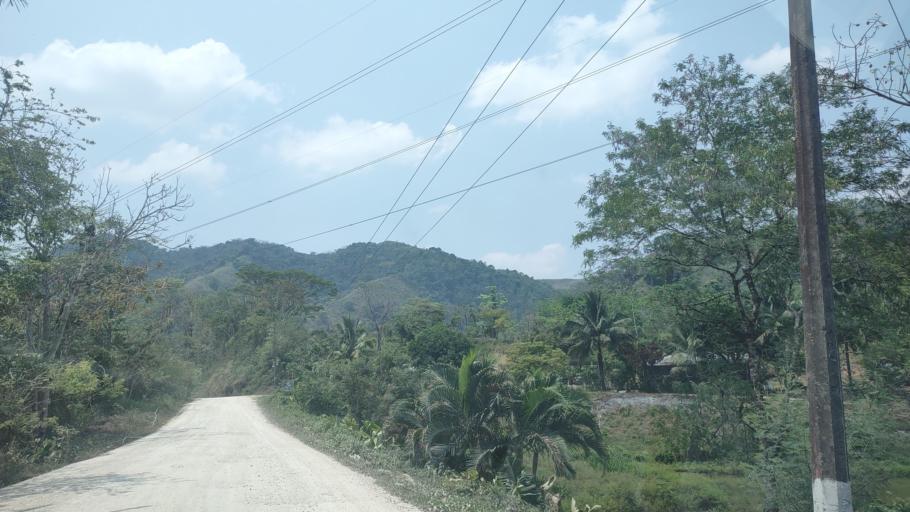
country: MX
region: Tabasco
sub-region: Huimanguillo
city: Francisco Rueda
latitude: 17.4945
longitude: -93.8442
